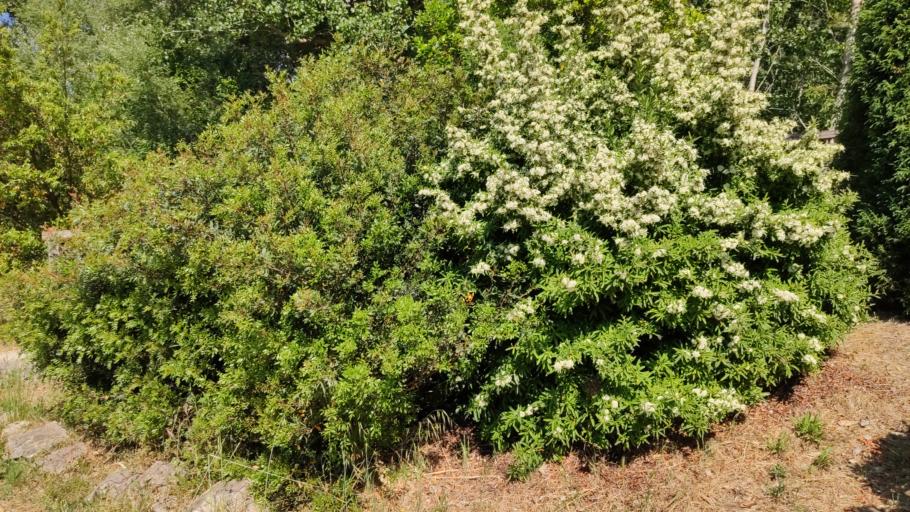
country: IT
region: Umbria
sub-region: Provincia di Terni
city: Amelia
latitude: 42.5602
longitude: 12.4188
